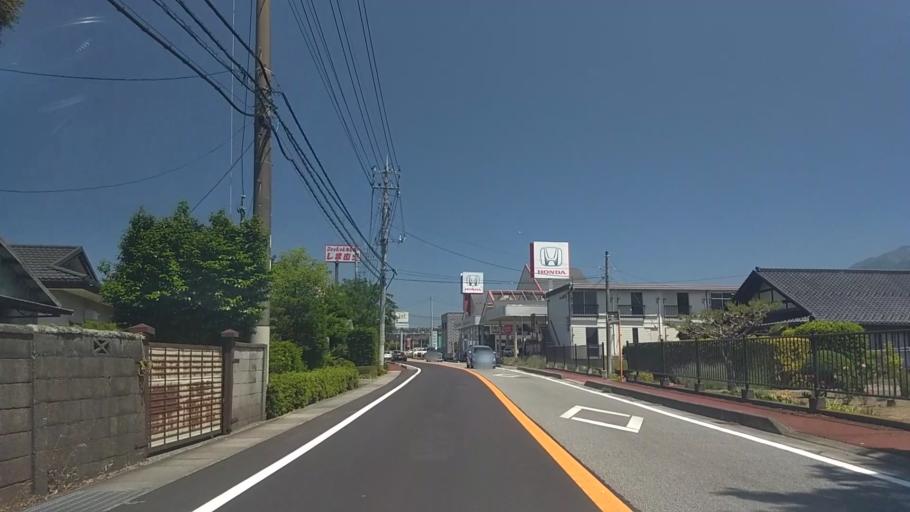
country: JP
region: Yamanashi
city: Nirasaki
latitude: 35.7263
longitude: 138.4493
